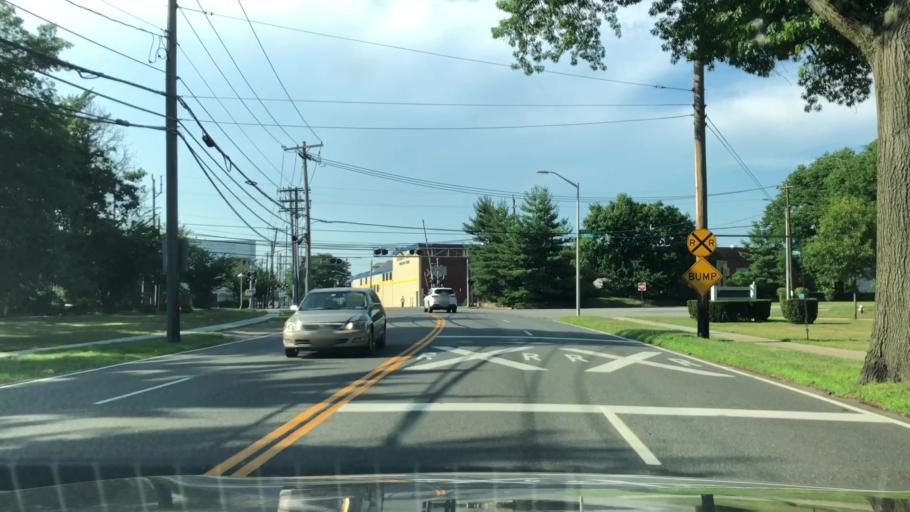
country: US
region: New York
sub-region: Nassau County
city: New Hyde Park
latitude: 40.7303
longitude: -73.6790
